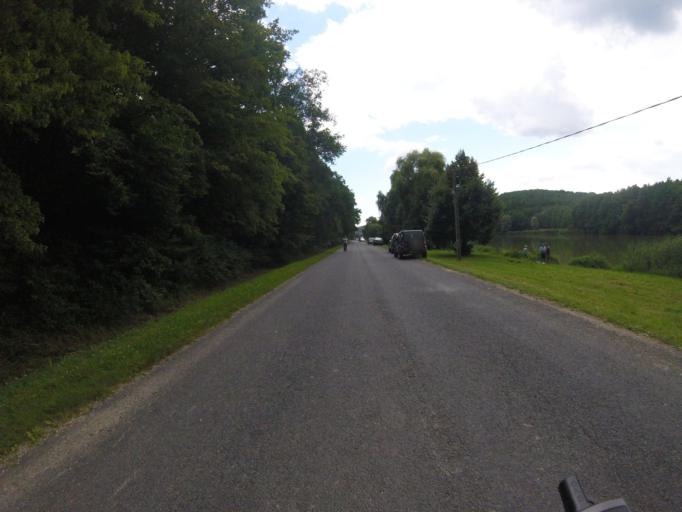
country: HU
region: Zala
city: Becsehely
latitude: 46.4979
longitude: 16.7405
